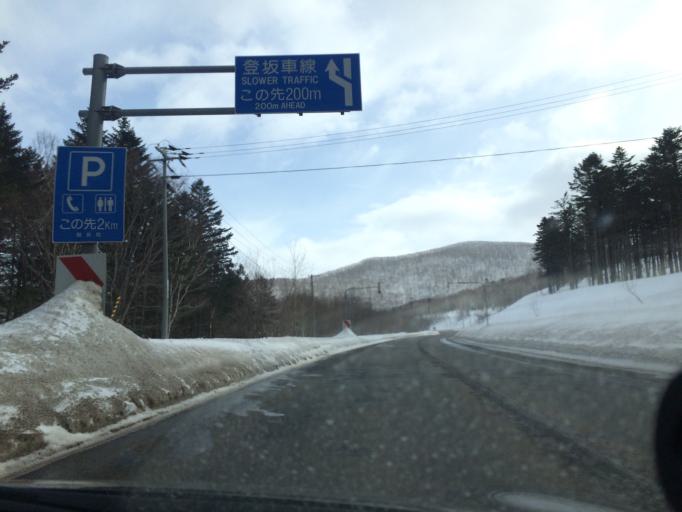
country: JP
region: Hokkaido
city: Shimo-furano
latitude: 43.1325
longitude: 142.7575
